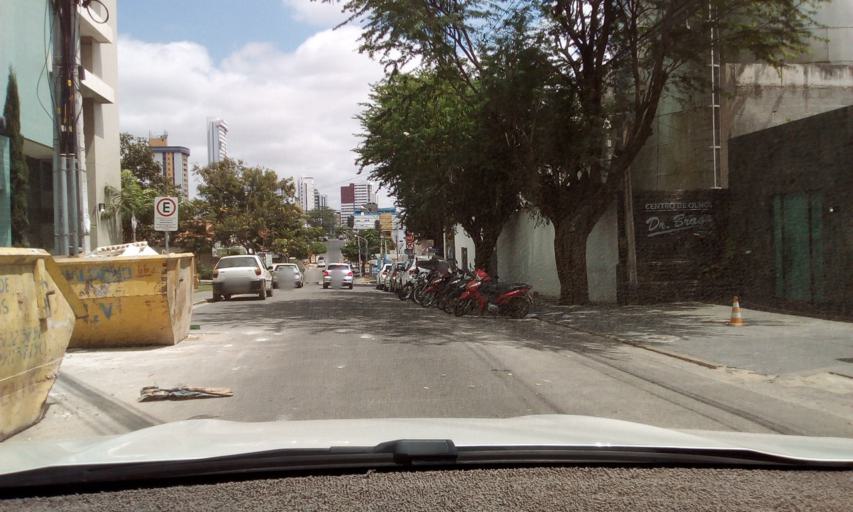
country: BR
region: Pernambuco
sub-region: Caruaru
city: Caruaru
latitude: -8.2776
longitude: -35.9711
